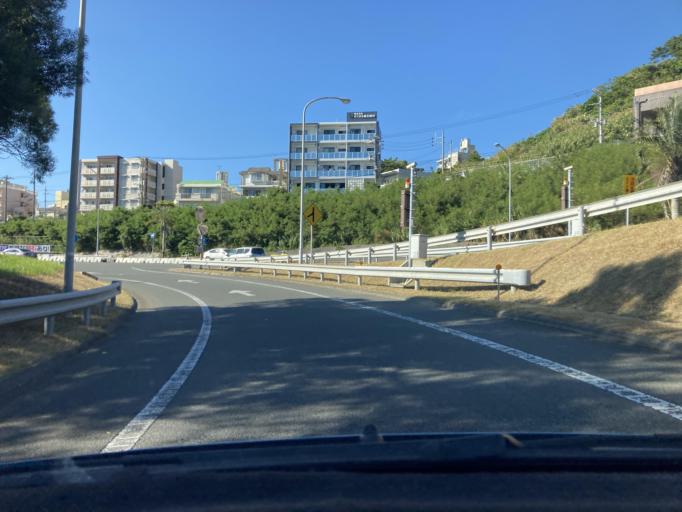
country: JP
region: Okinawa
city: Ginowan
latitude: 26.2484
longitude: 127.7497
